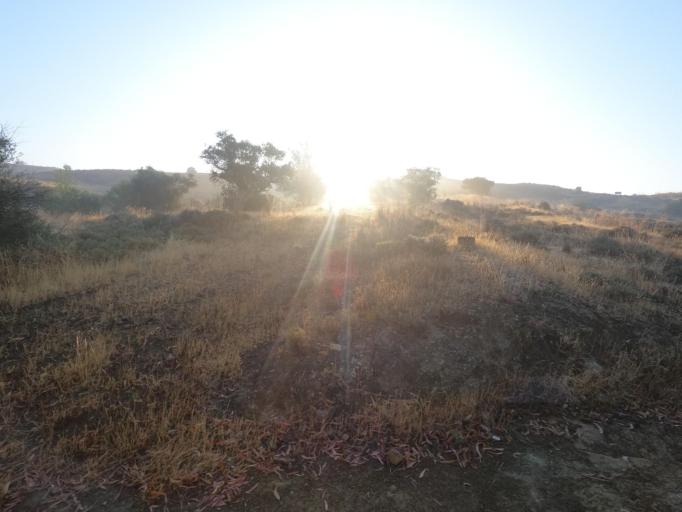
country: CY
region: Larnaka
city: Mosfiloti
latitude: 34.9753
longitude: 33.4200
